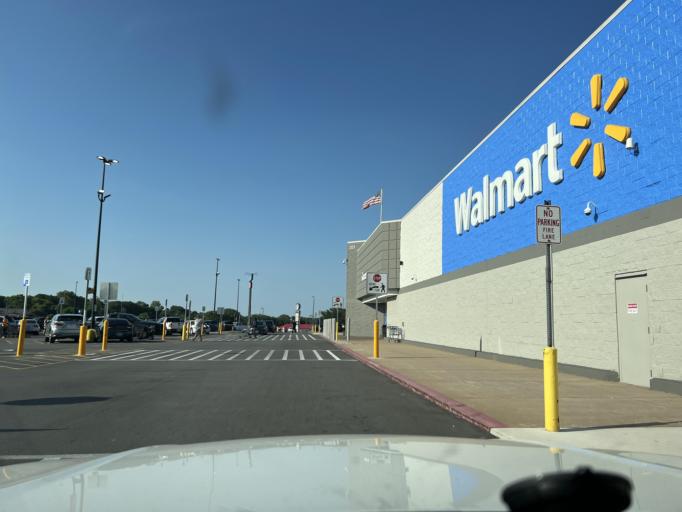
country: US
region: Texas
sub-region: Washington County
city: Brenham
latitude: 30.1401
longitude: -96.3938
